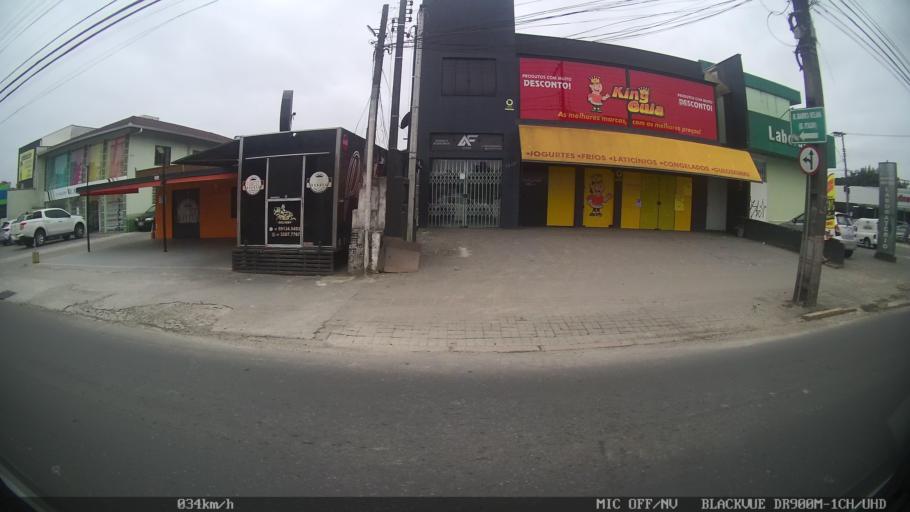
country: BR
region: Santa Catarina
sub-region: Joinville
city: Joinville
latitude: -26.3377
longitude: -48.8475
